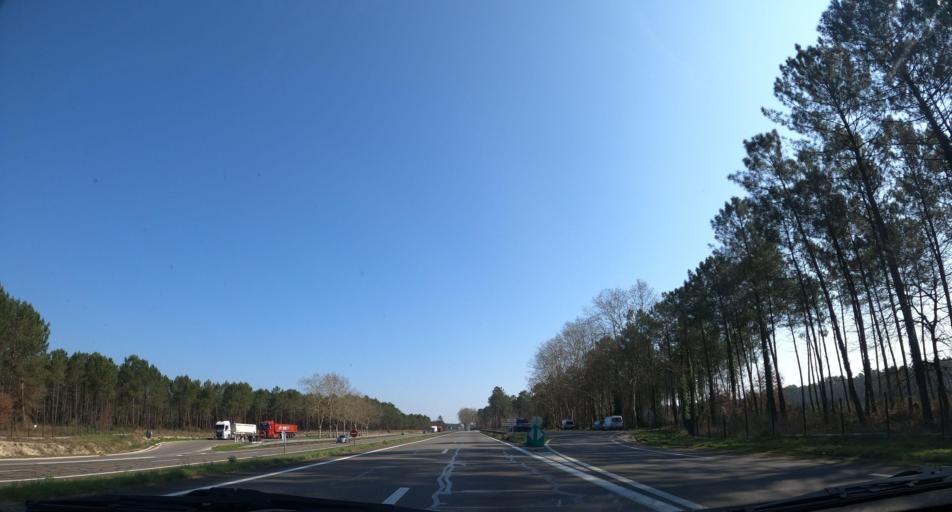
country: FR
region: Aquitaine
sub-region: Departement des Landes
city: Riviere-Saas-et-Gourby
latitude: 43.7040
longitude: -1.1760
